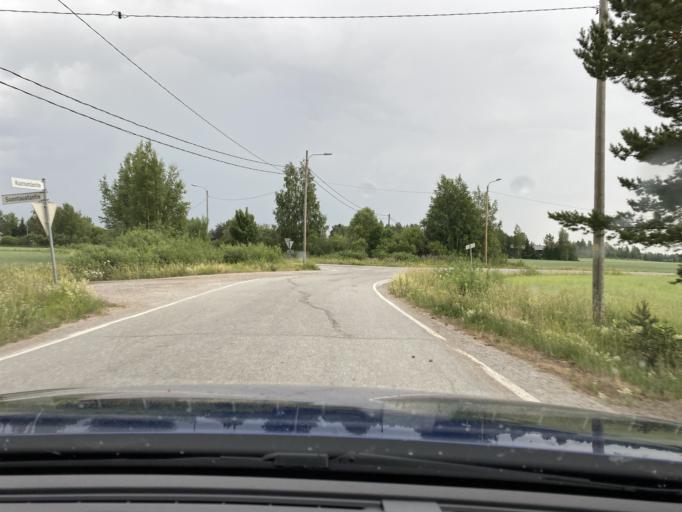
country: FI
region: Satakunta
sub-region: Rauma
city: Eura
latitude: 61.1471
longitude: 22.1270
